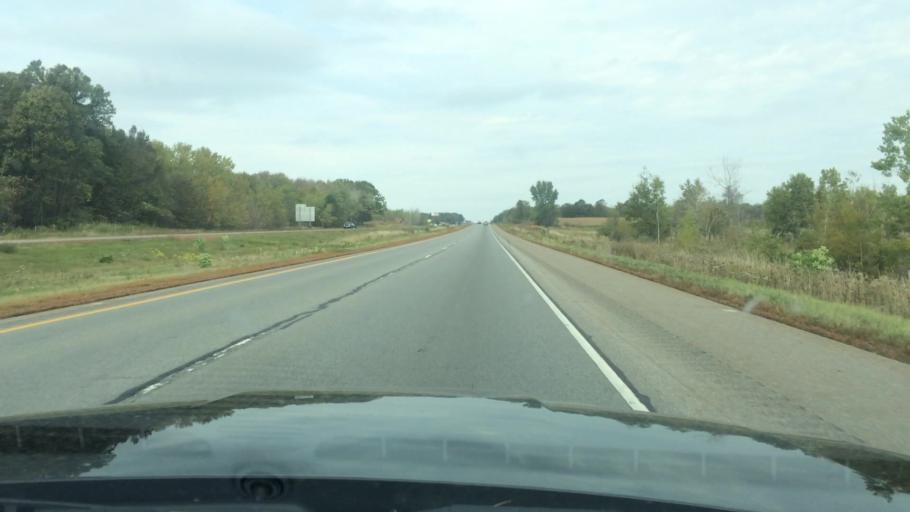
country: US
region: Wisconsin
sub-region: Marathon County
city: Mosinee
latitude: 44.7471
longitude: -89.6797
